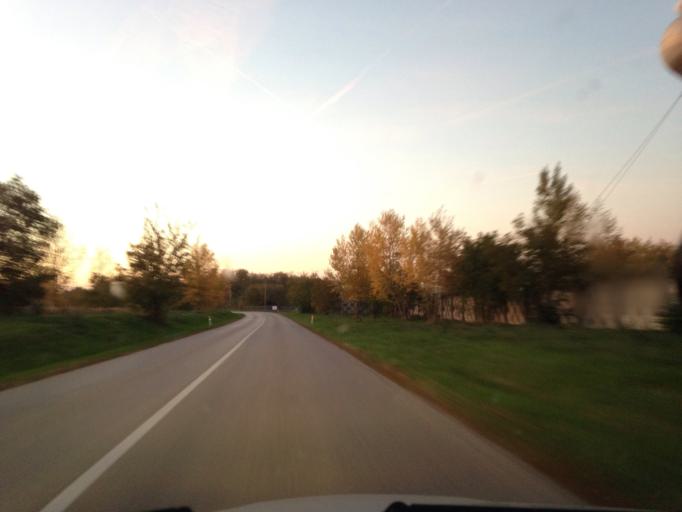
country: SK
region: Nitriansky
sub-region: Okres Komarno
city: Hurbanovo
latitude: 47.8618
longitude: 18.2729
